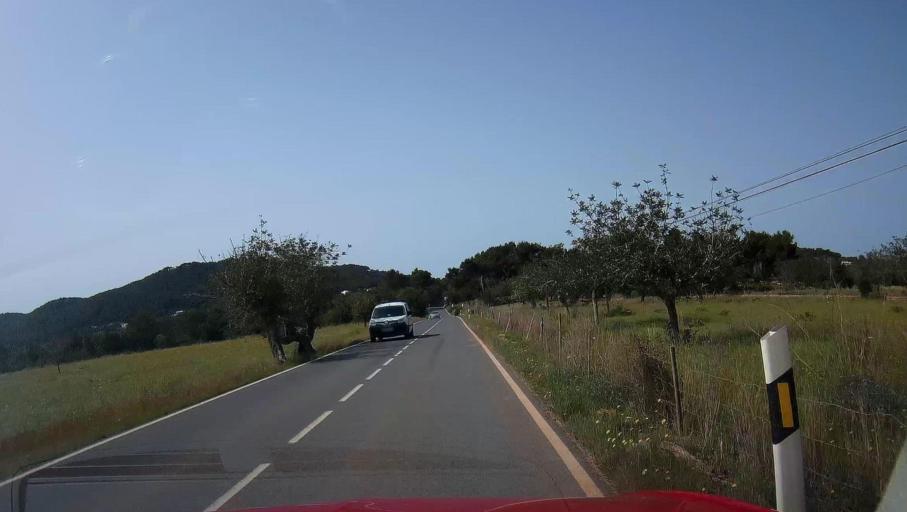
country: ES
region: Balearic Islands
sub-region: Illes Balears
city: Sant Joan de Labritja
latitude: 39.0494
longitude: 1.5716
